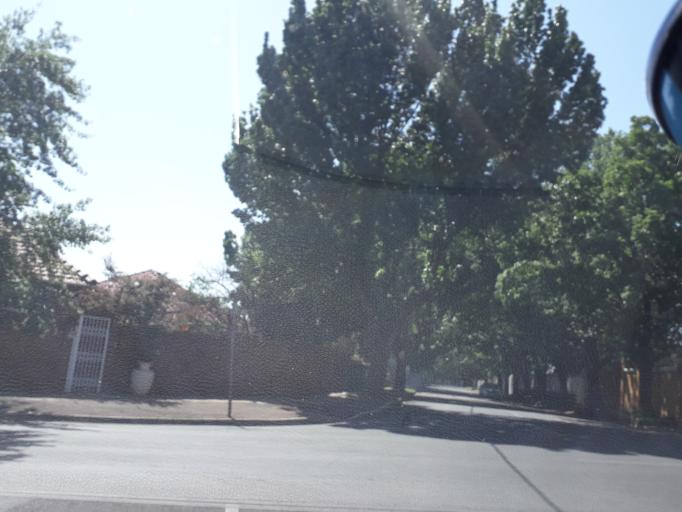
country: ZA
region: Gauteng
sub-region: City of Johannesburg Metropolitan Municipality
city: Johannesburg
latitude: -26.1484
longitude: 28.0157
